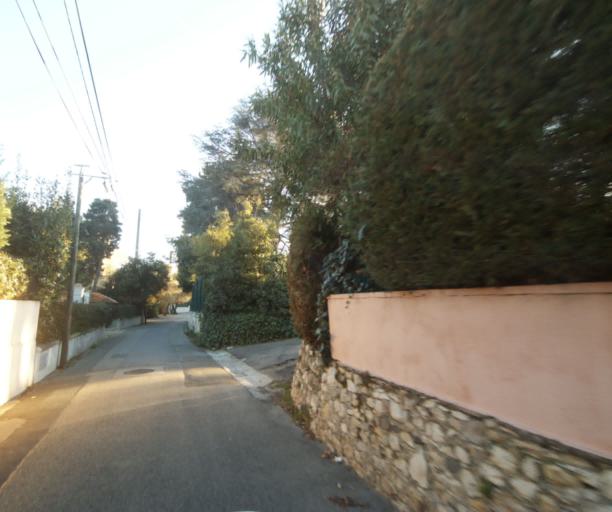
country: FR
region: Provence-Alpes-Cote d'Azur
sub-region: Departement des Alpes-Maritimes
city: Antibes
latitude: 43.5683
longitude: 7.1268
